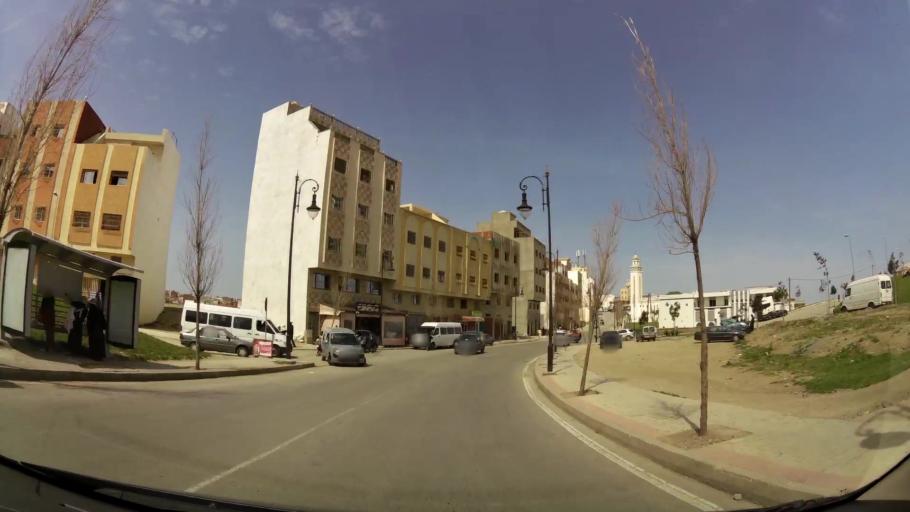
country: MA
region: Tanger-Tetouan
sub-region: Tanger-Assilah
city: Tangier
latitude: 35.7358
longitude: -5.8214
